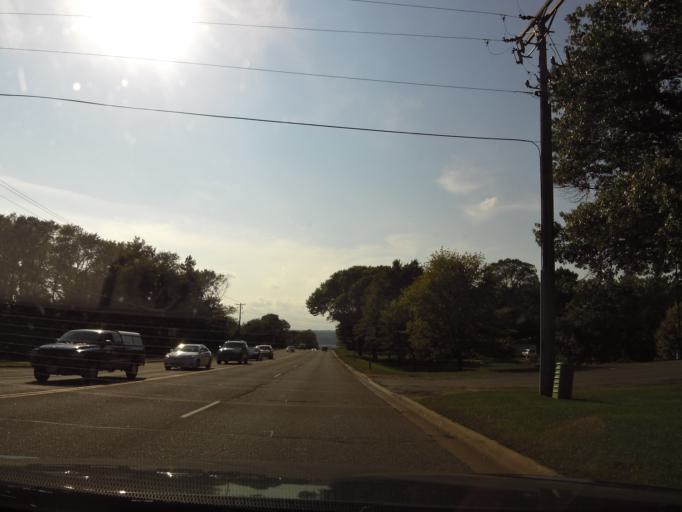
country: US
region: Minnesota
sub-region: Washington County
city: Newport
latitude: 44.8885
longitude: -92.9919
